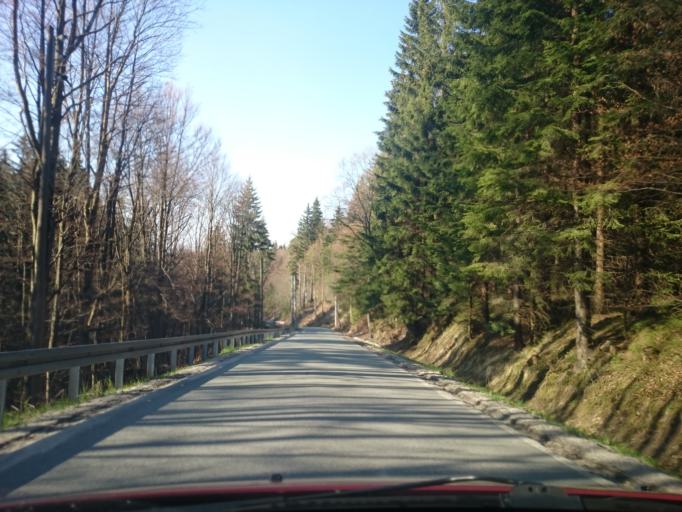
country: PL
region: Lower Silesian Voivodeship
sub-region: Powiat klodzki
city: Duszniki-Zdroj
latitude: 50.3333
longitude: 16.4055
